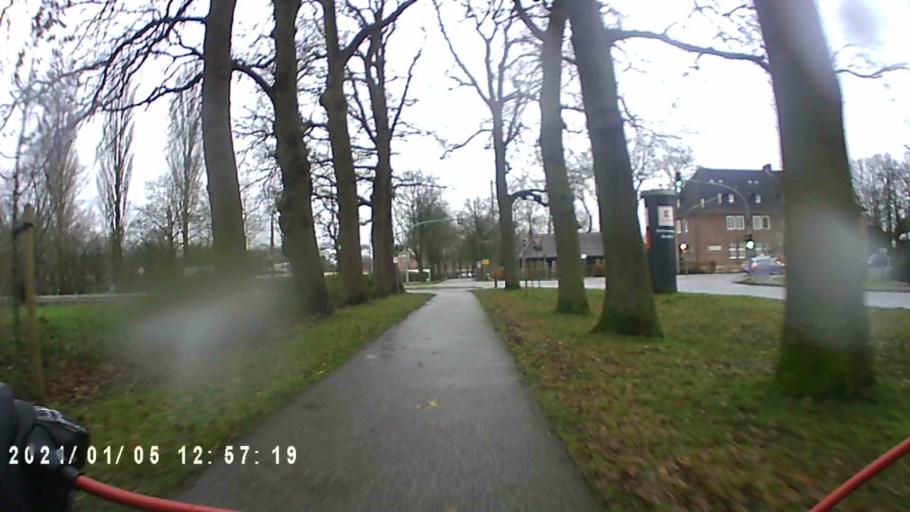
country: DE
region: Lower Saxony
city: Leer
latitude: 53.2299
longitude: 7.4783
